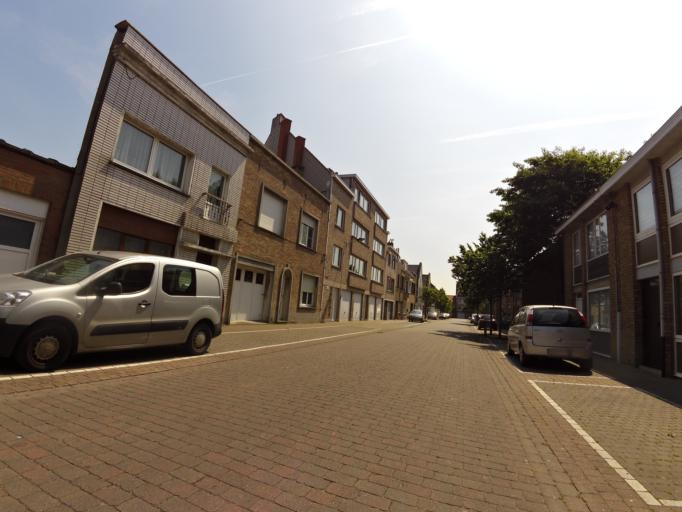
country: BE
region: Flanders
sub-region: Provincie West-Vlaanderen
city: Ostend
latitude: 51.2172
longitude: 2.9008
